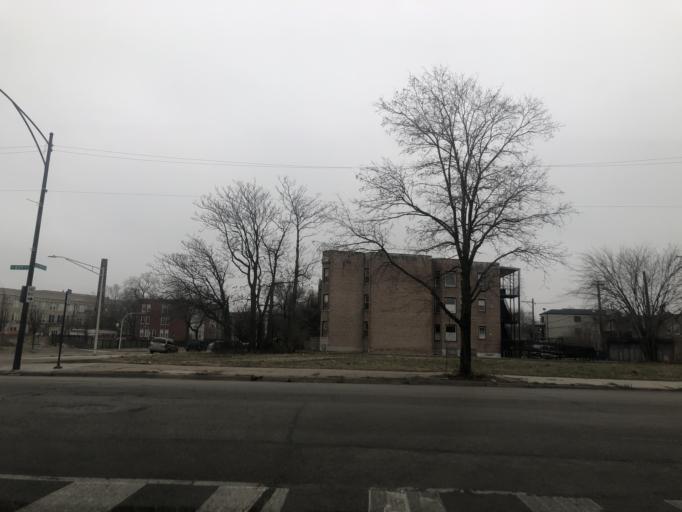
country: US
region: Illinois
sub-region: Cook County
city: Chicago
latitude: 41.7807
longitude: -87.5994
